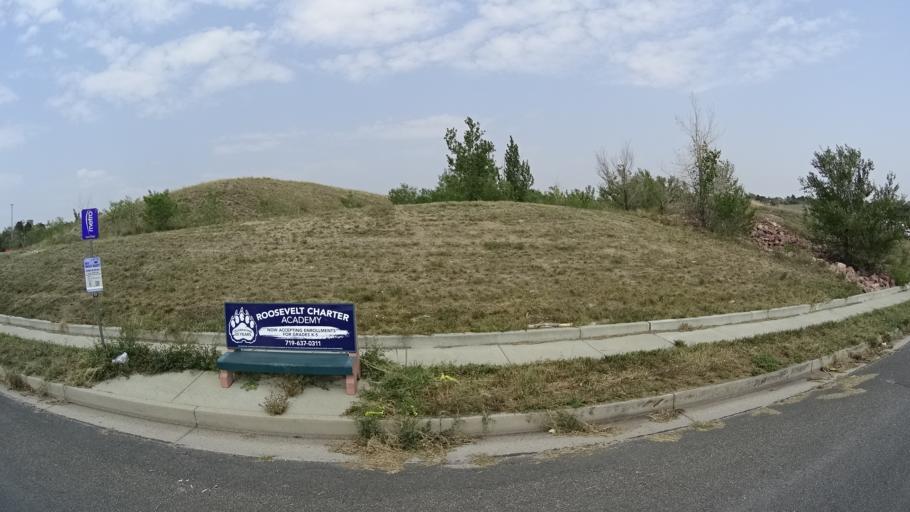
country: US
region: Colorado
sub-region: El Paso County
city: Colorado Springs
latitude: 38.8288
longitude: -104.7881
